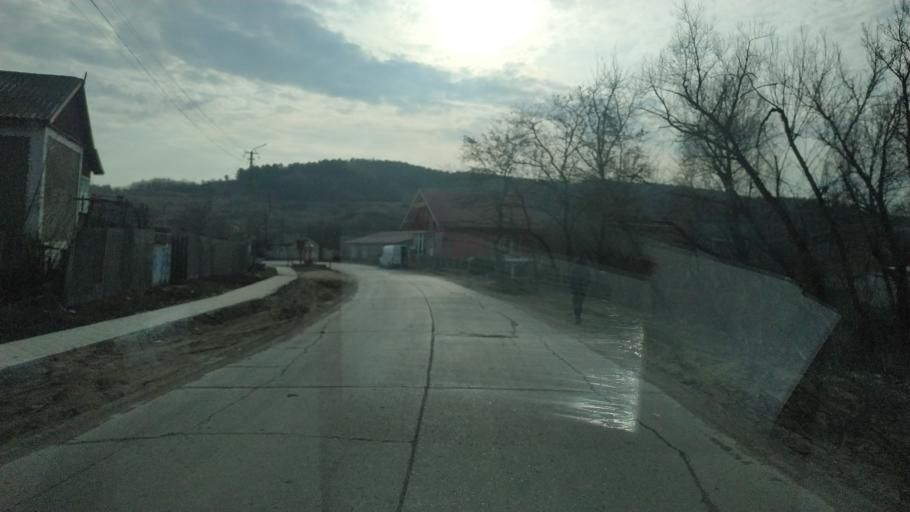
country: MD
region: Chisinau
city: Vadul lui Voda
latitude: 47.0066
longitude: 29.1221
